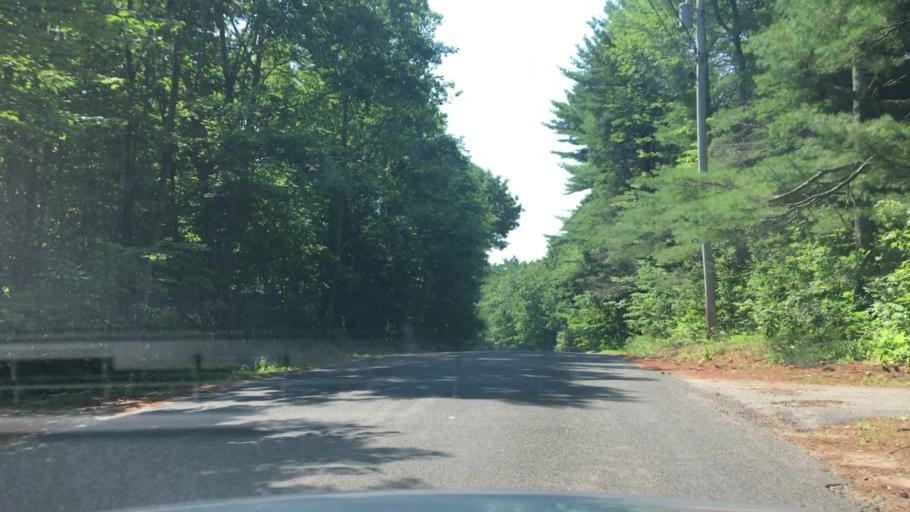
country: US
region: Maine
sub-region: Androscoggin County
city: Greene
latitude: 44.2258
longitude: -70.1052
